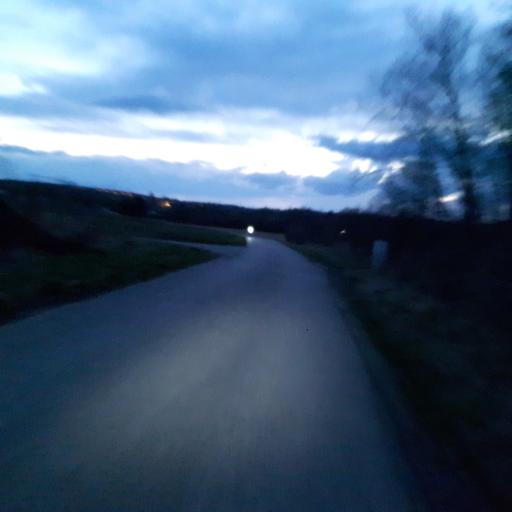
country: DE
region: Baden-Wuerttemberg
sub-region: Regierungsbezirk Stuttgart
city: Walheim
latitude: 49.0050
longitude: 9.1617
